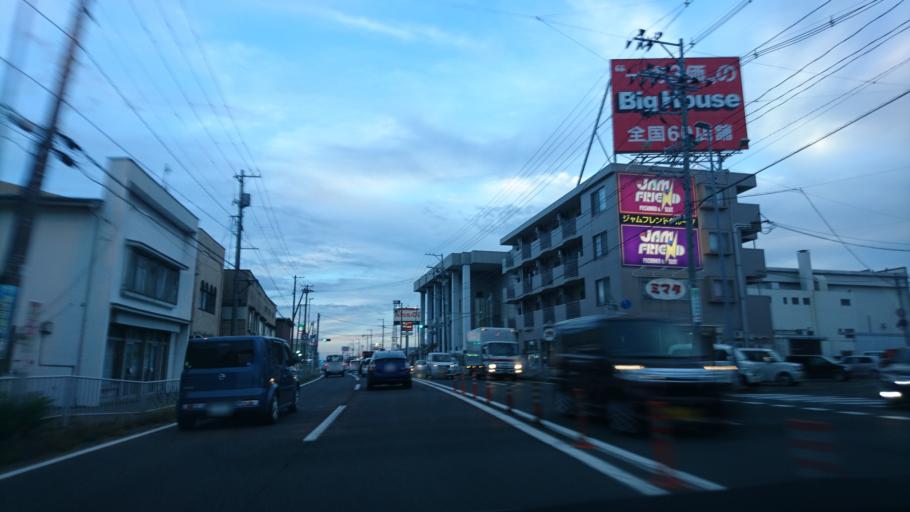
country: JP
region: Iwate
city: Morioka-shi
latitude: 39.6722
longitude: 141.1557
